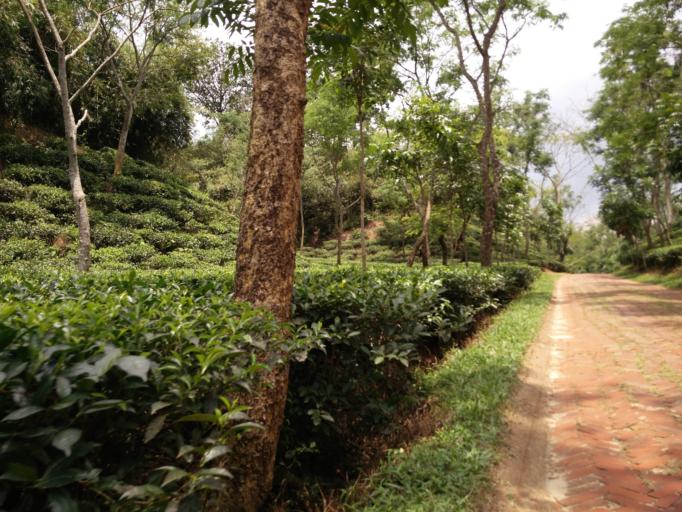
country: IN
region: Tripura
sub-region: Dhalai
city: Kamalpur
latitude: 24.3003
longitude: 91.7985
